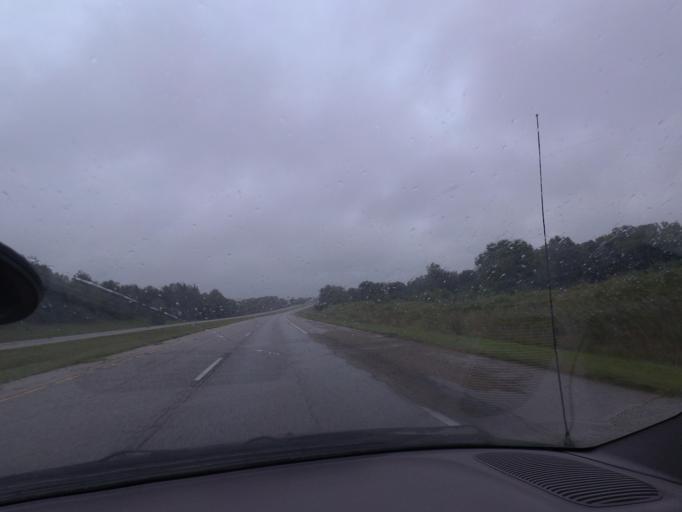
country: US
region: Illinois
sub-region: Pike County
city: Pittsfield
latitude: 39.6862
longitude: -90.8840
